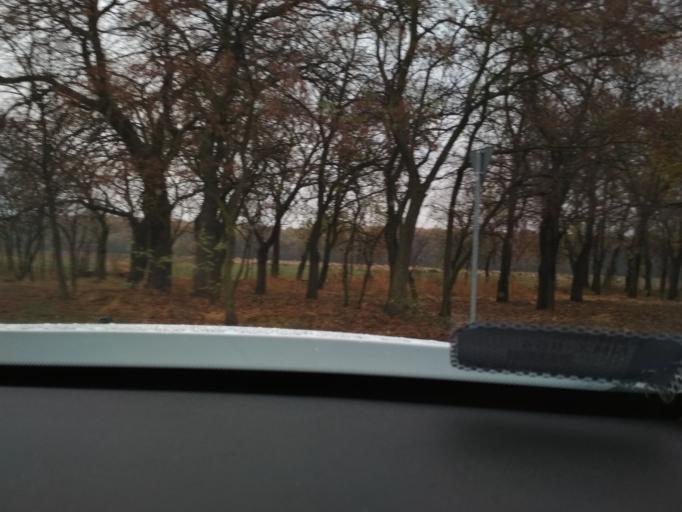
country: HU
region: Csongrad
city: Opusztaszer
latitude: 46.4369
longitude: 20.1414
